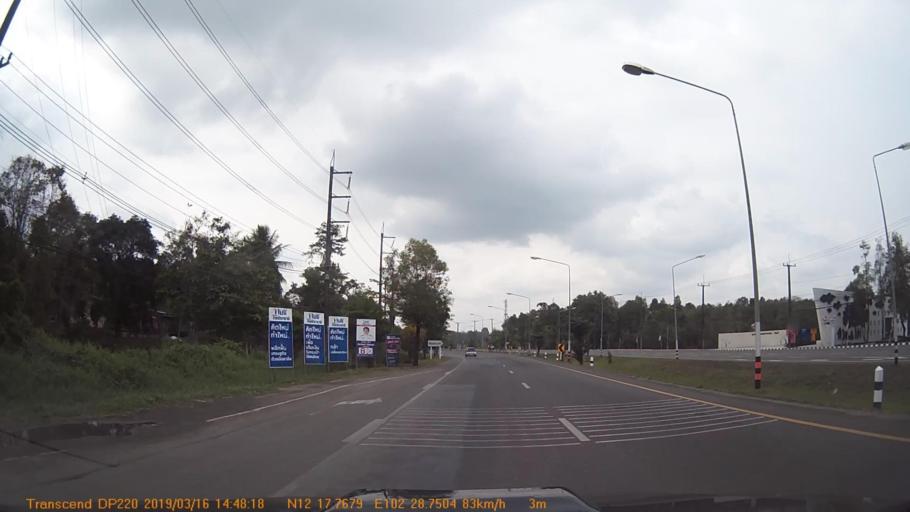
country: TH
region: Trat
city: Trat
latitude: 12.2964
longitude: 102.4790
